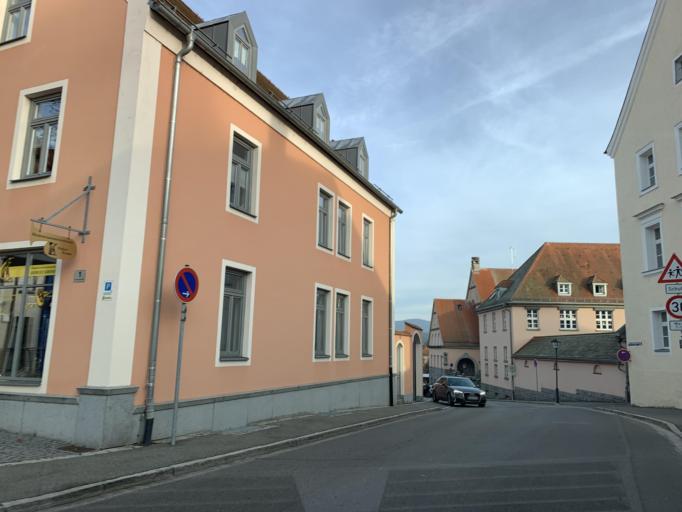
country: DE
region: Bavaria
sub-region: Upper Palatinate
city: Neunburg vorm Wald
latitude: 49.3482
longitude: 12.3894
